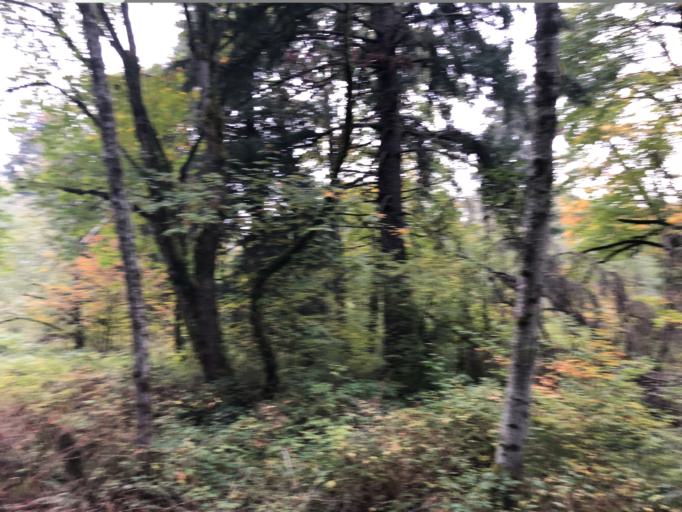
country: US
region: Washington
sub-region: King County
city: Snoqualmie
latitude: 47.5344
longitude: -121.8245
